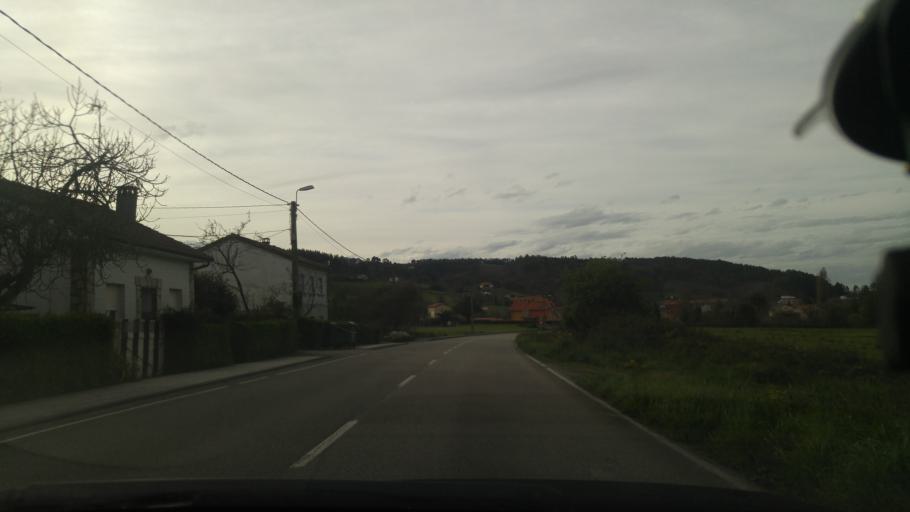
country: ES
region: Asturias
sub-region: Province of Asturias
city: Corvera de Asturias
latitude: 43.5044
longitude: -5.8649
